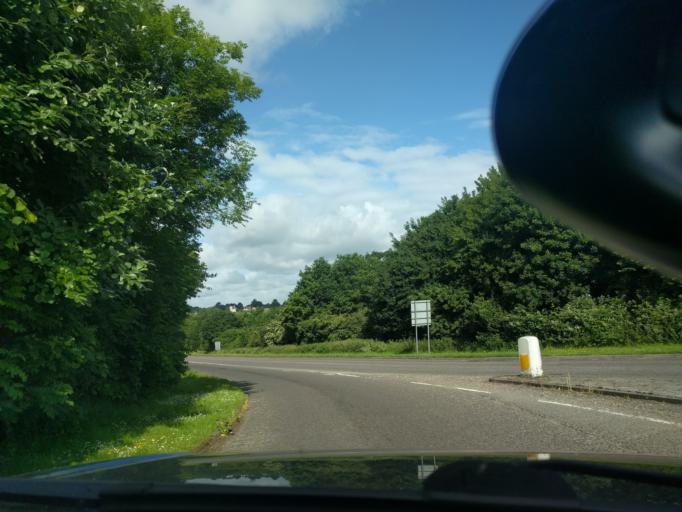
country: GB
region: England
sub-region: Wiltshire
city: Chippenham
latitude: 51.4529
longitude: -2.1124
